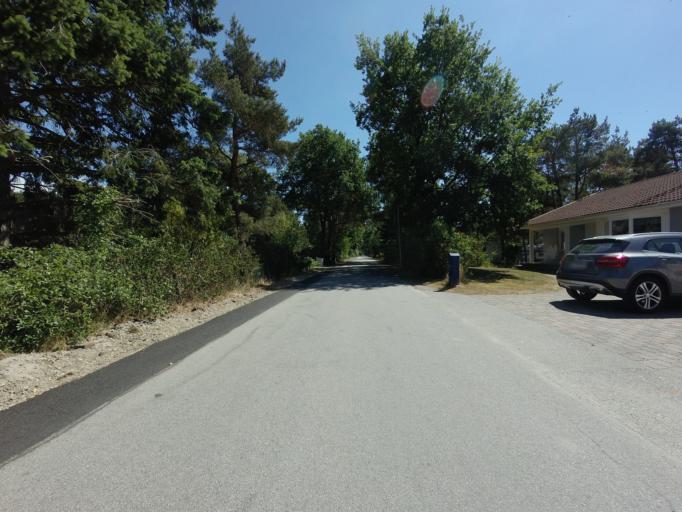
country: SE
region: Skane
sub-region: Vellinge Kommun
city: Ljunghusen
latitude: 55.4012
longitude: 12.9385
